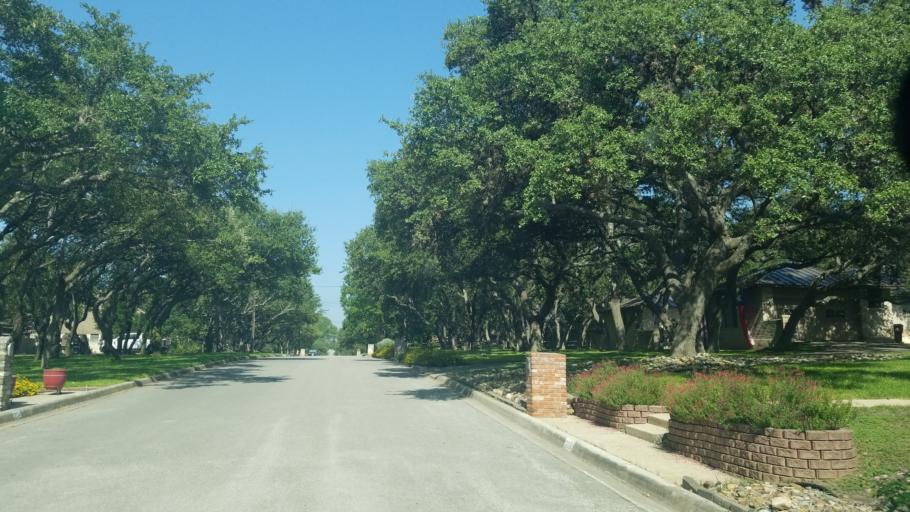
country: US
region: Texas
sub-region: Bexar County
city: Hollywood Park
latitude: 29.6052
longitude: -98.4783
